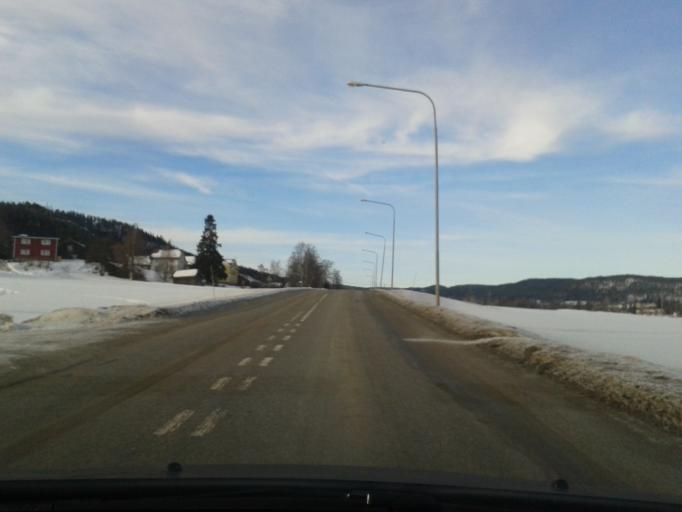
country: SE
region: Vaesternorrland
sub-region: OErnskoeldsviks Kommun
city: Bredbyn
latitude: 63.4994
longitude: 18.0808
